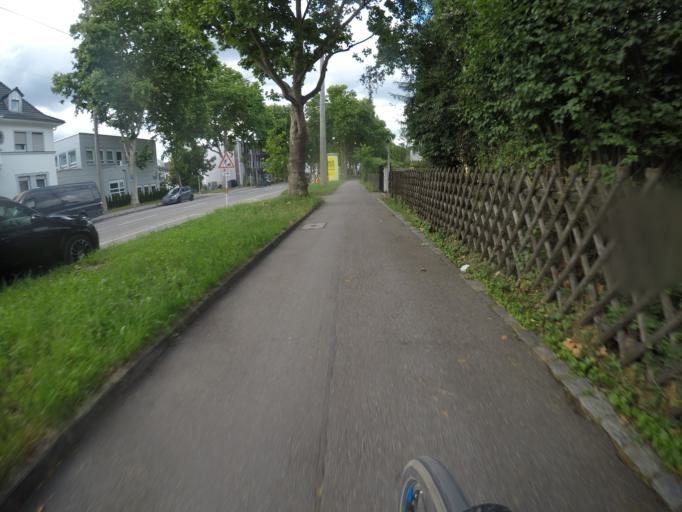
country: DE
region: Baden-Wuerttemberg
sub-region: Regierungsbezirk Stuttgart
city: Fellbach
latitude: 48.7692
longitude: 9.2637
